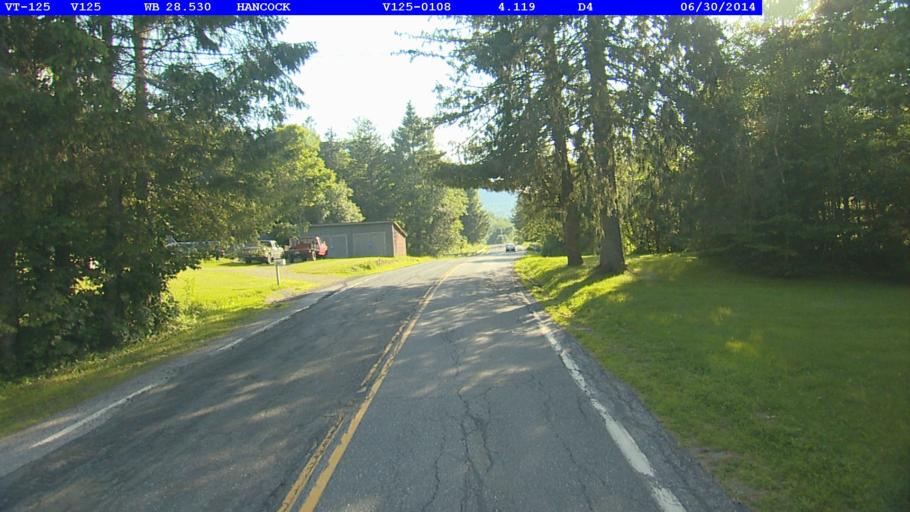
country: US
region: Vermont
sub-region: Rutland County
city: Brandon
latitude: 43.9286
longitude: -72.9008
